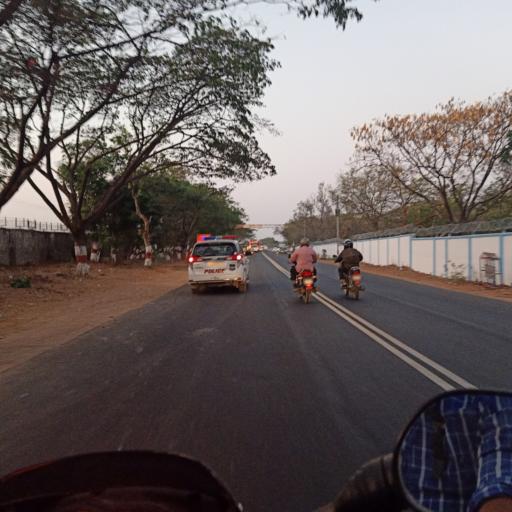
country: IN
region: Telangana
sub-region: Rangareddi
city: Secunderabad
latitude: 17.5521
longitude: 78.5361
